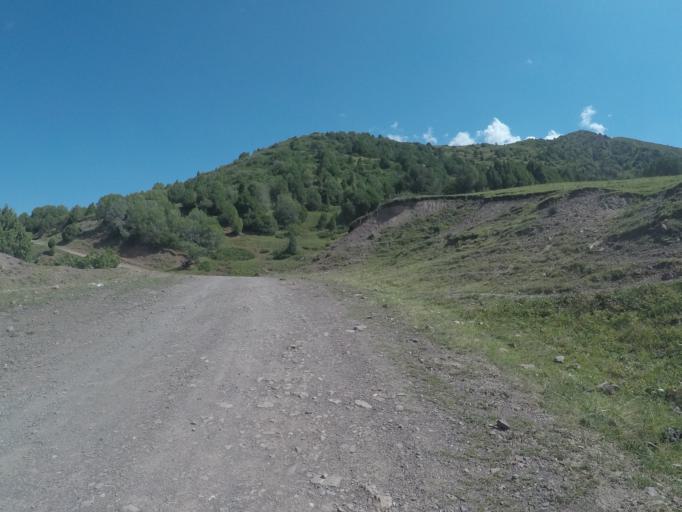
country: KG
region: Chuy
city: Bishkek
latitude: 42.6464
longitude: 74.5587
